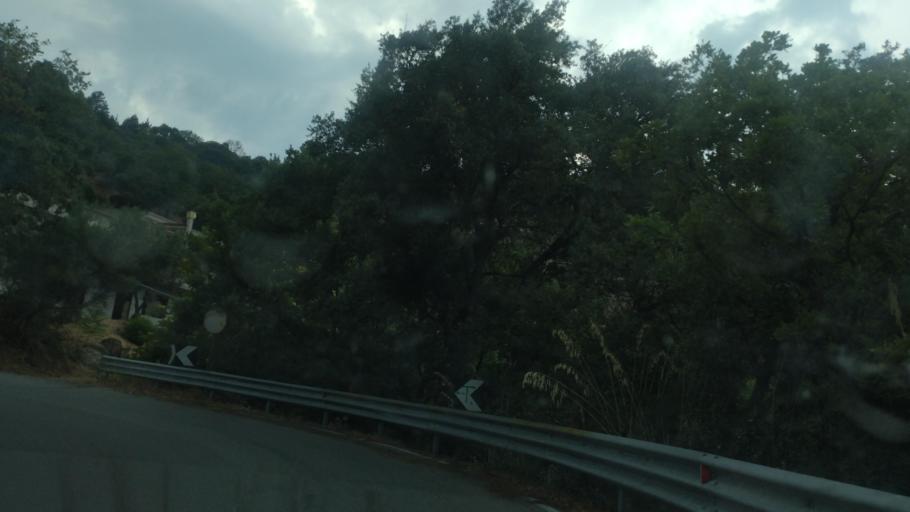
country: IT
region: Calabria
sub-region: Provincia di Catanzaro
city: Squillace Lido
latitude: 38.7609
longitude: 16.5645
